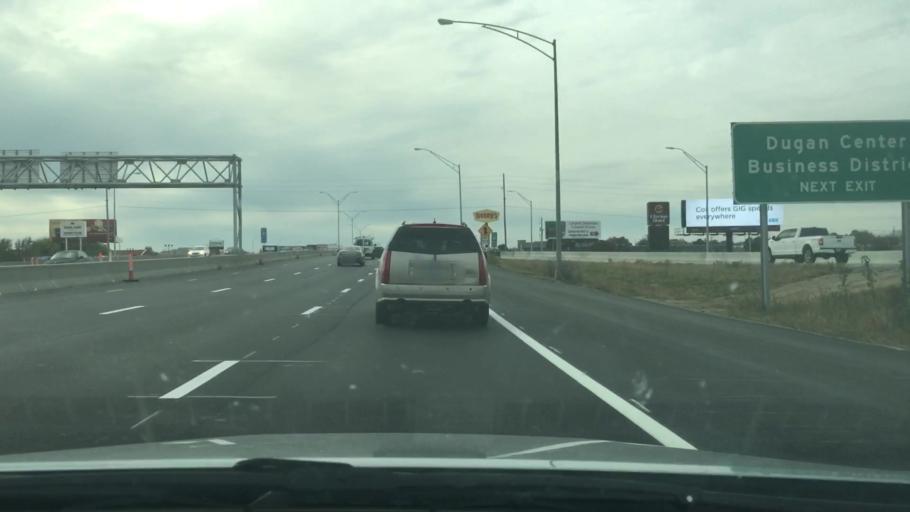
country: US
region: Kansas
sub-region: Sedgwick County
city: Wichita
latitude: 37.6732
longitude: -97.4063
